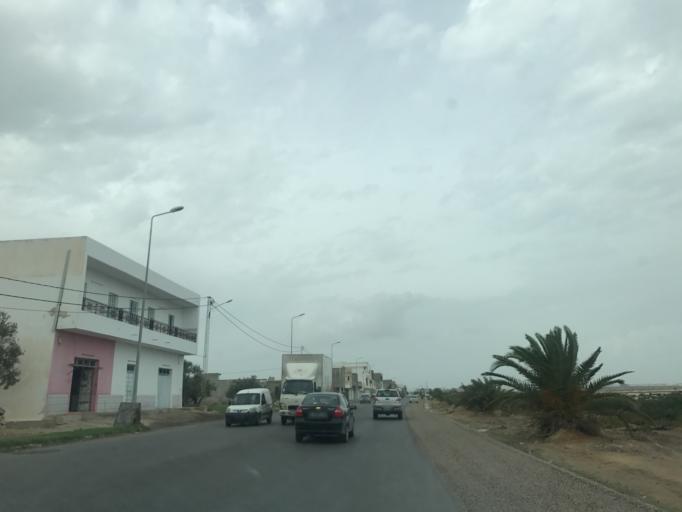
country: TN
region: Al Munastir
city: Qusaybat al Madyuni
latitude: 35.7042
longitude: 10.8256
